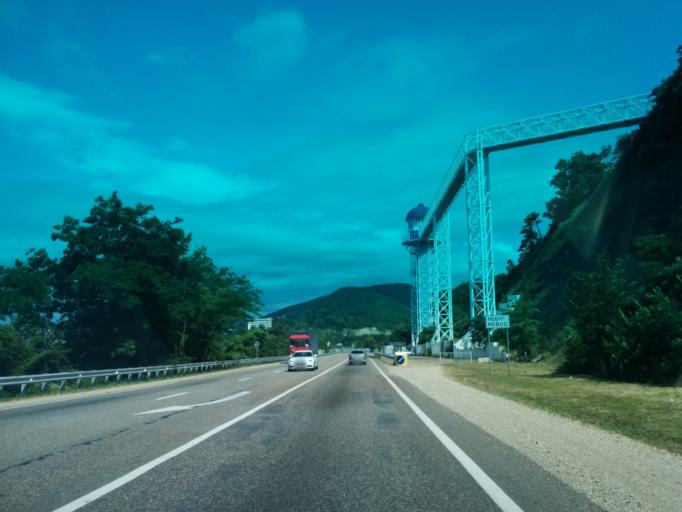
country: RU
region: Krasnodarskiy
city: Nebug
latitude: 44.1566
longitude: 39.0045
